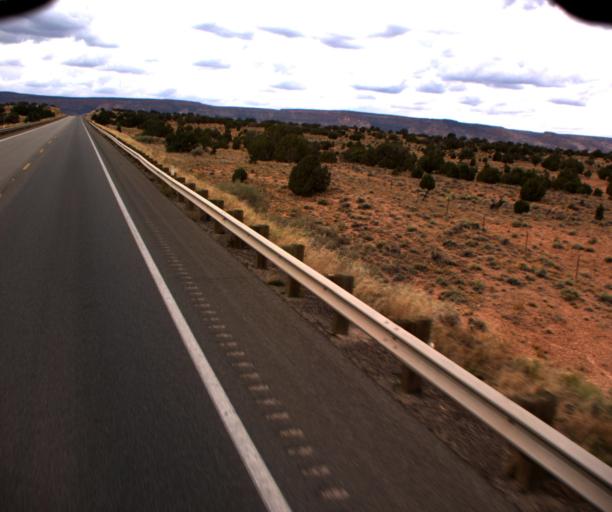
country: US
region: Arizona
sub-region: Navajo County
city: Kayenta
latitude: 36.6991
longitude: -110.3135
